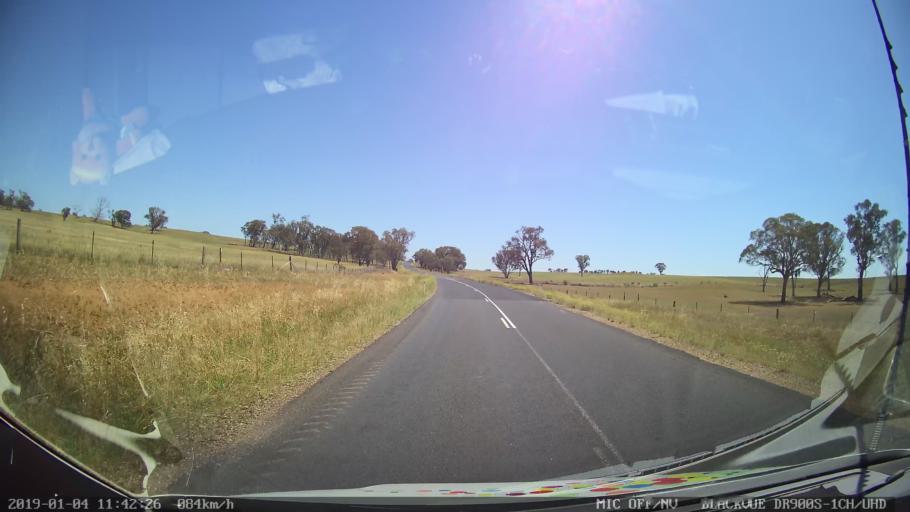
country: AU
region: New South Wales
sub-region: Cabonne
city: Molong
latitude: -32.9816
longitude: 148.7867
